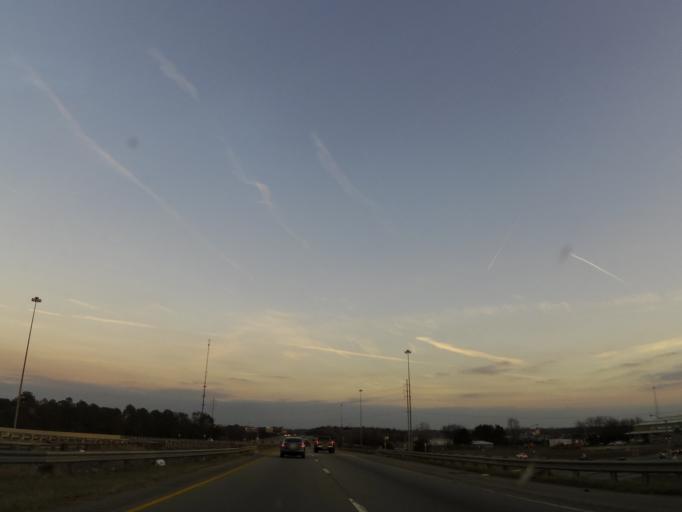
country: US
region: Georgia
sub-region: Dougherty County
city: Albany
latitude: 31.6069
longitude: -84.1553
